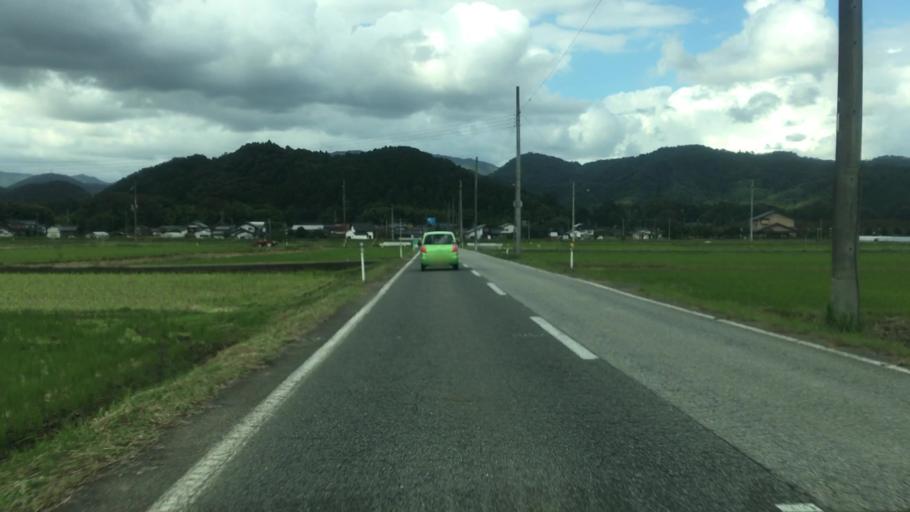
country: JP
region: Hyogo
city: Toyooka
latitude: 35.4502
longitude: 134.7295
